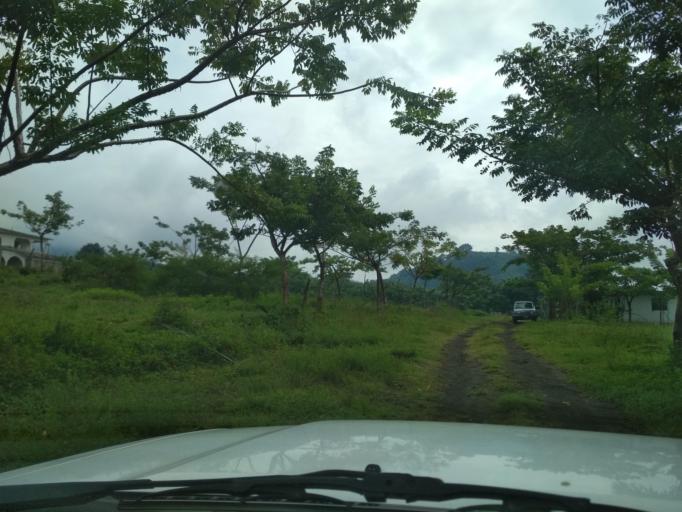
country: MX
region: Veracruz
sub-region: San Andres Tuxtla
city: Matacapan
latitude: 18.4403
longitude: -95.1489
